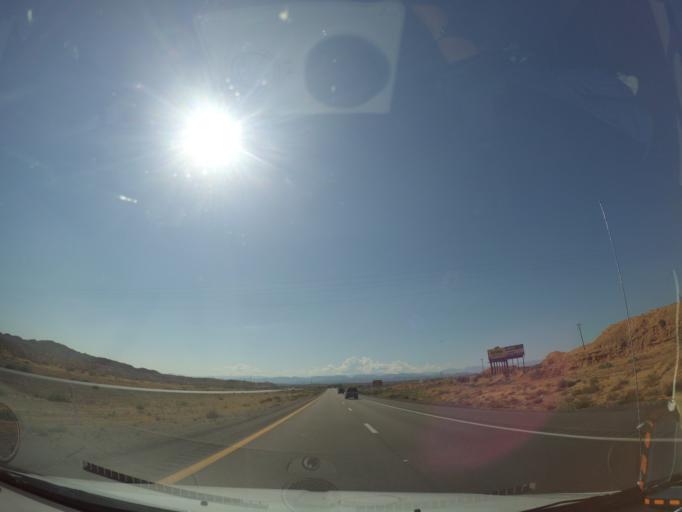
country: US
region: Nevada
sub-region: Clark County
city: Moapa Town
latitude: 36.6660
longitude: -114.5563
